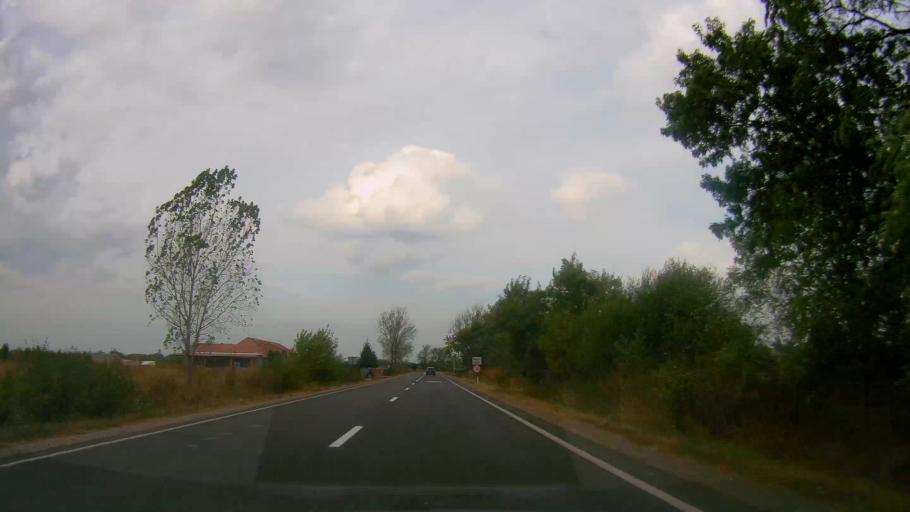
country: RO
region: Satu Mare
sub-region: Comuna Acas
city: Acas
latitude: 47.5404
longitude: 22.7944
